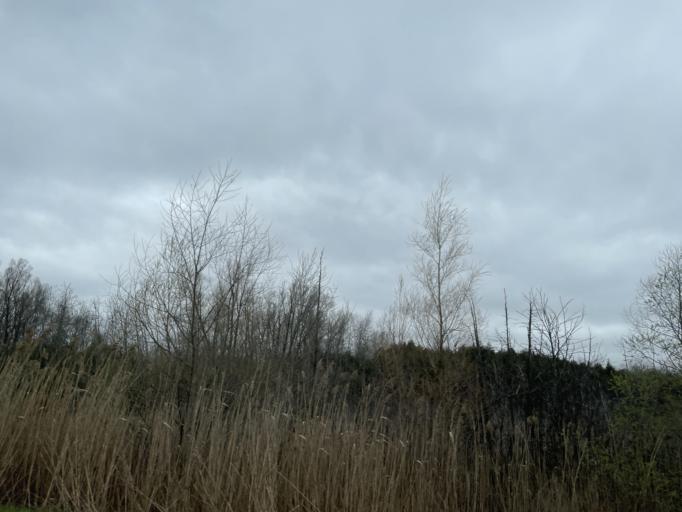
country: CA
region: Ontario
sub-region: Wellington County
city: Guelph
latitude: 43.5748
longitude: -80.2198
